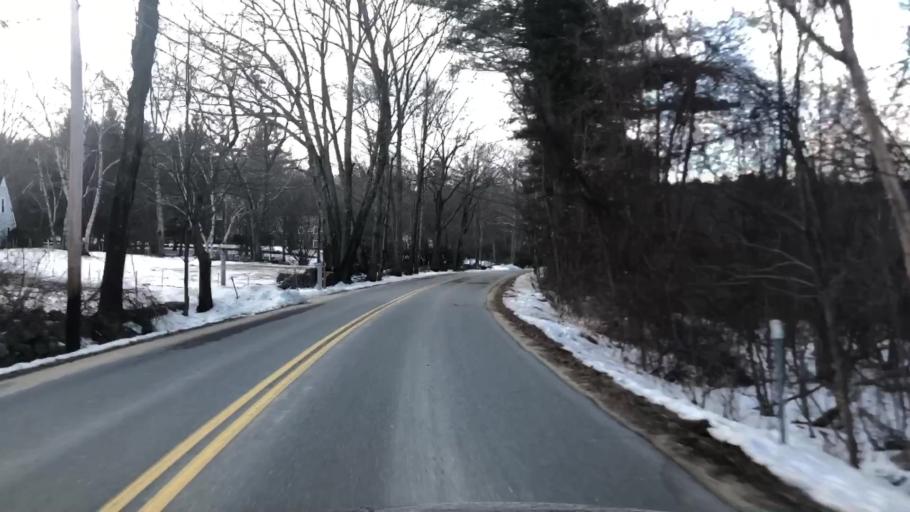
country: US
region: New Hampshire
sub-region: Hillsborough County
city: Milford
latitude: 42.8629
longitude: -71.6342
